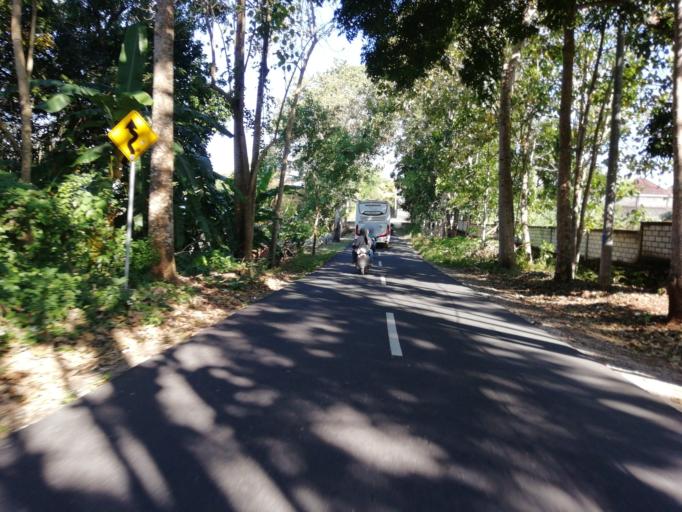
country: ID
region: Bali
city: Jimbaran
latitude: -8.8316
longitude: 115.1772
